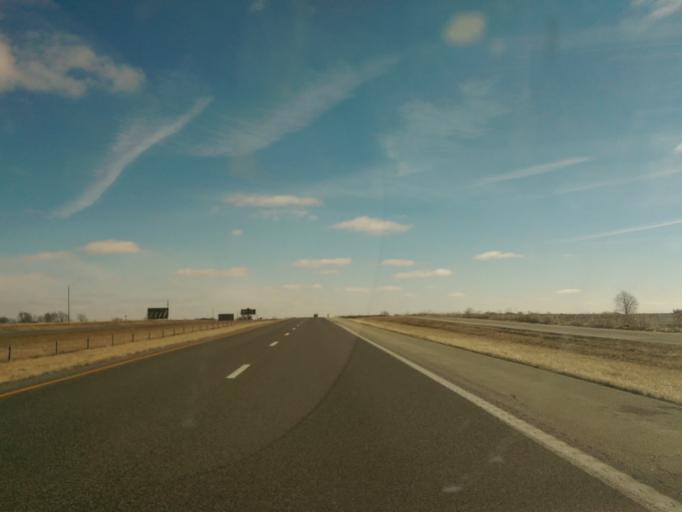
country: US
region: Missouri
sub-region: Callaway County
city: Fulton
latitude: 38.9422
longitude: -91.8754
